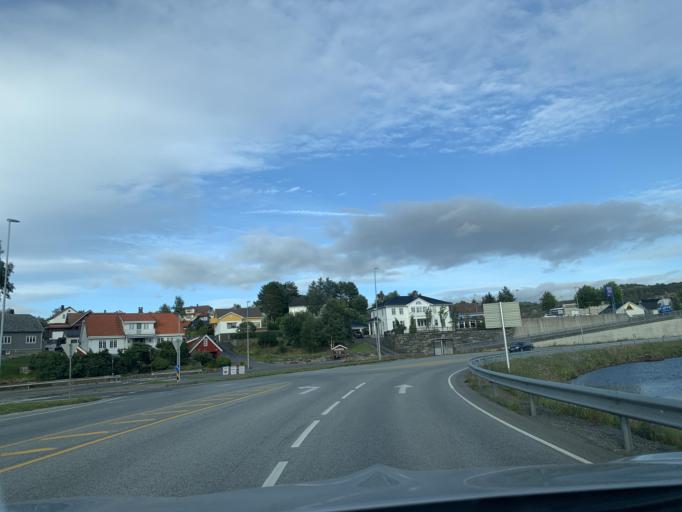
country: NO
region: Rogaland
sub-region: Eigersund
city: Egersund
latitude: 58.4617
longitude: 6.0100
